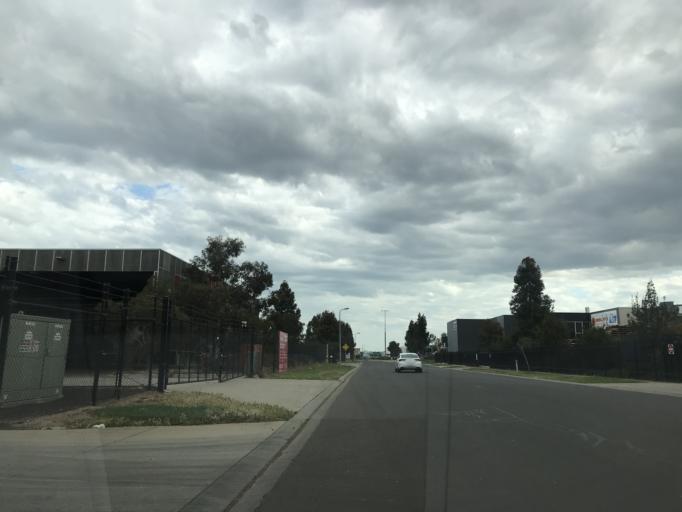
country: AU
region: Victoria
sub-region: Wyndham
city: Truganina
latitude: -37.8198
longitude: 144.7450
